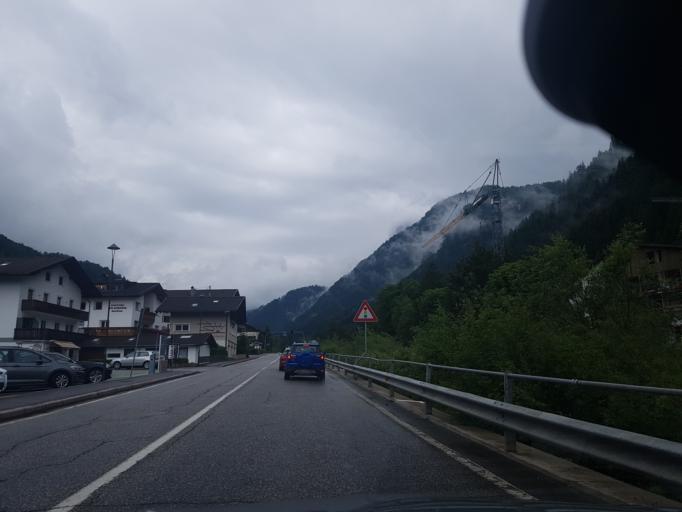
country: IT
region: Trentino-Alto Adige
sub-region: Bolzano
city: Ortisei
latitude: 46.5715
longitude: 11.6768
